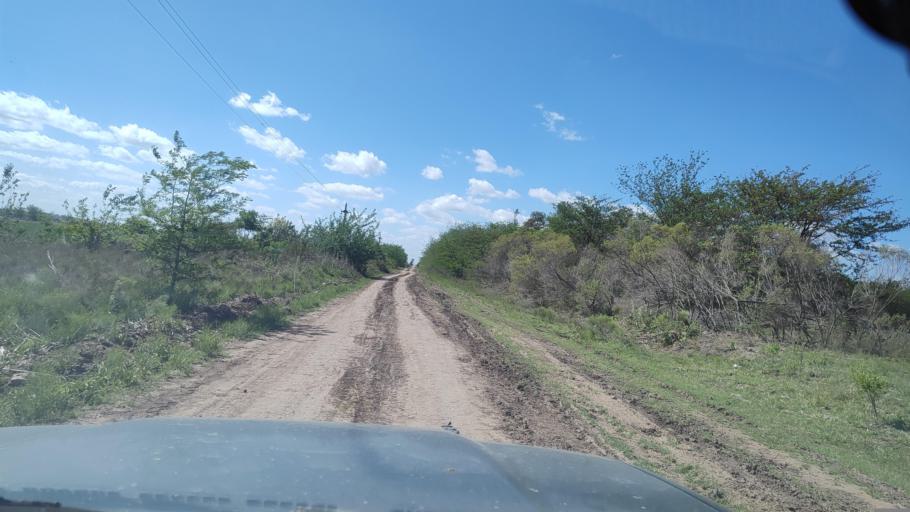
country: AR
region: Buenos Aires
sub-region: Partido de Lujan
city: Lujan
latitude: -34.5286
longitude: -59.1525
